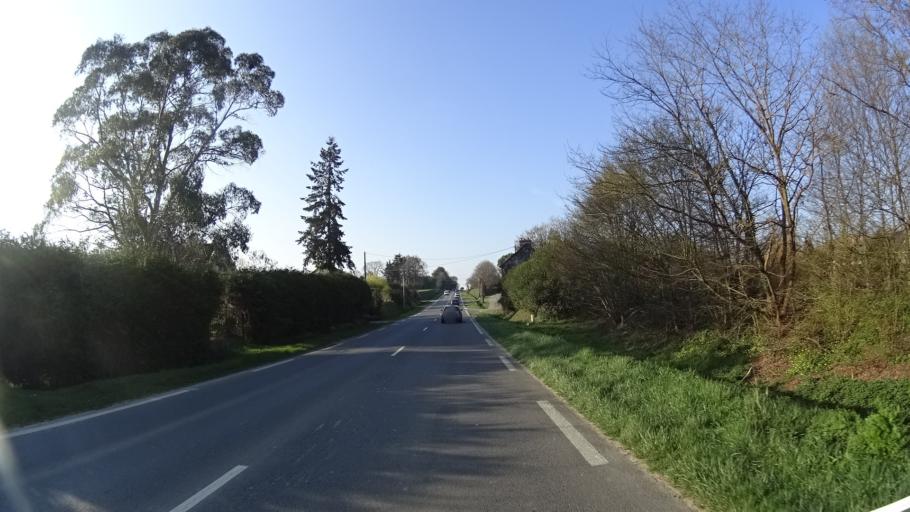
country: FR
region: Brittany
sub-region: Departement d'Ille-et-Vilaine
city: Melesse
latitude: 48.2039
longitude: -1.6954
